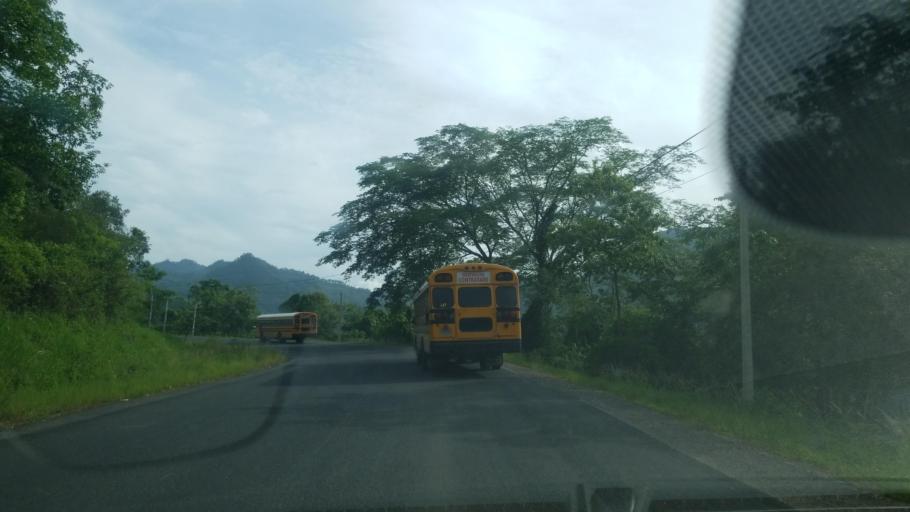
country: HN
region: Santa Barbara
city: Petoa
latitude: 15.2023
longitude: -88.2704
